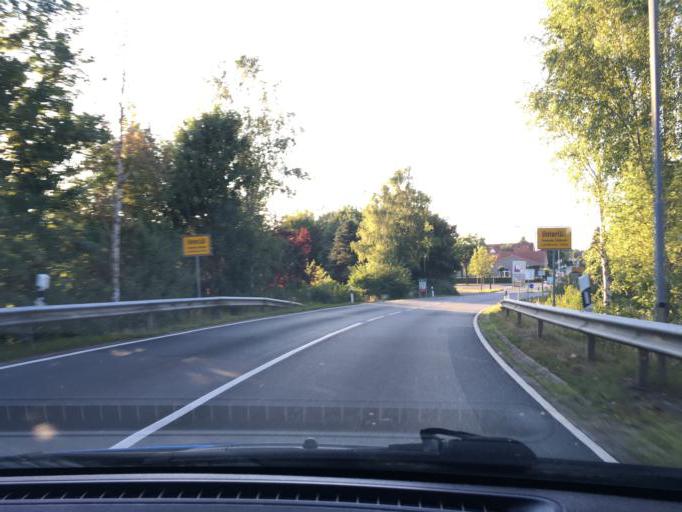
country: DE
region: Lower Saxony
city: Unterluss
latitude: 52.8328
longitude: 10.2969
